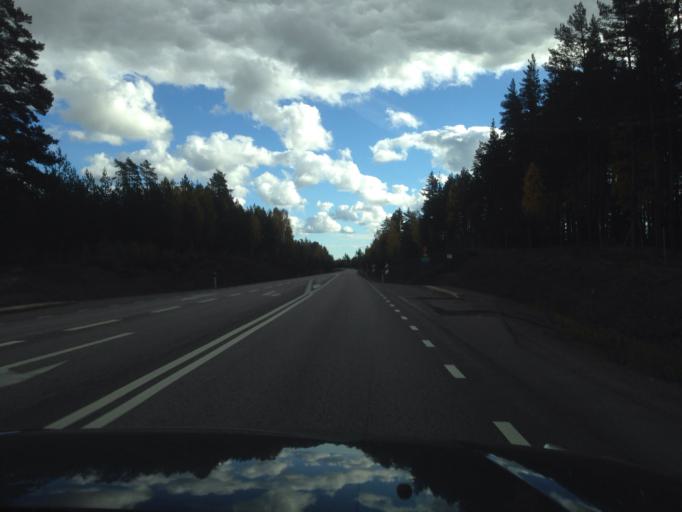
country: SE
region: Dalarna
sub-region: Hedemora Kommun
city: Langshyttan
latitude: 60.5501
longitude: 16.1240
